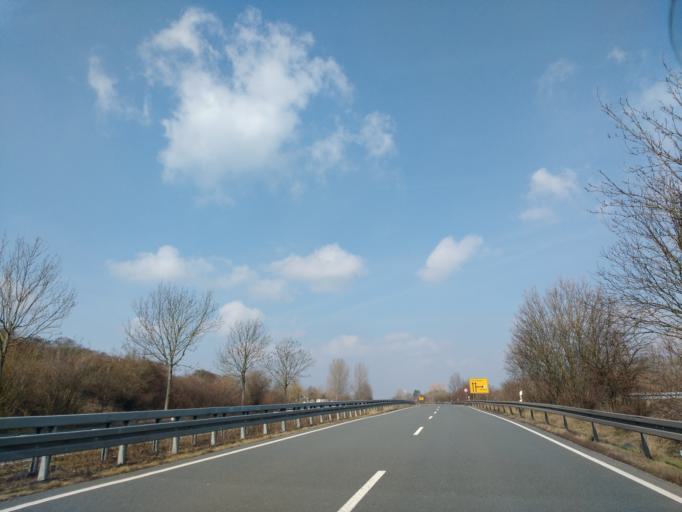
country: DE
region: Saxony-Anhalt
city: Roblingen am See
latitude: 51.4820
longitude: 11.7064
